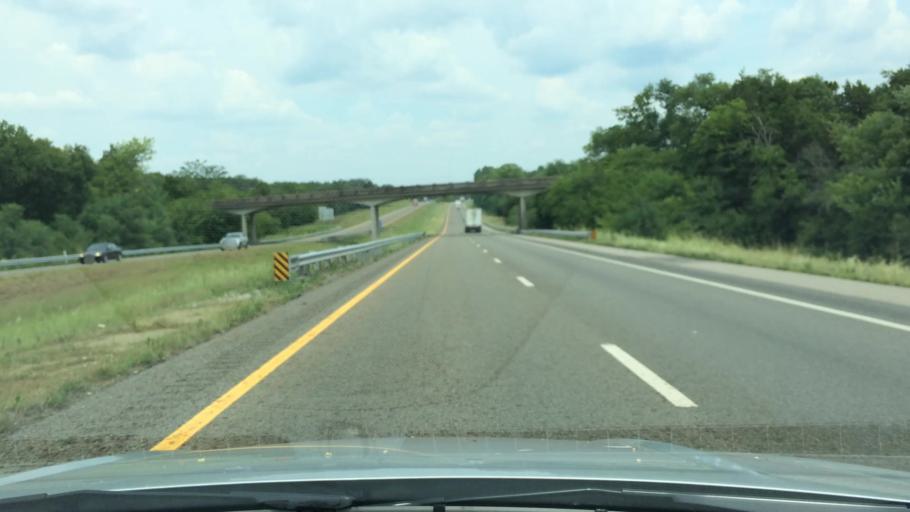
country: US
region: Tennessee
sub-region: Marshall County
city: Lewisburg
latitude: 35.5419
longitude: -86.9054
